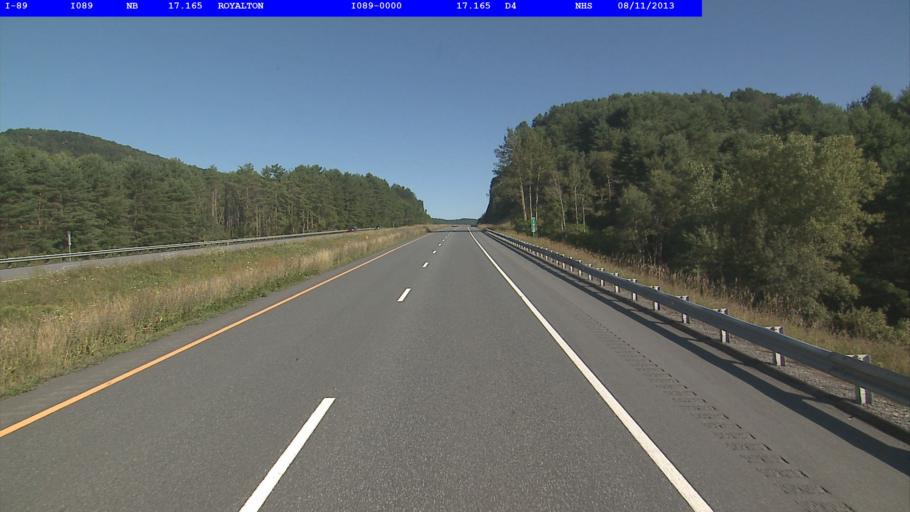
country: US
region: Vermont
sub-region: Windsor County
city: Woodstock
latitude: 43.8036
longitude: -72.5139
